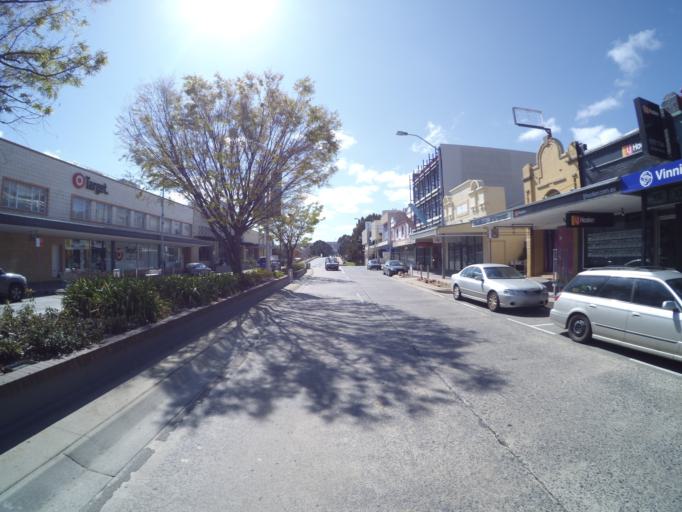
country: AU
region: New South Wales
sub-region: Queanbeyan
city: Queanbeyan
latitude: -35.3529
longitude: 149.2353
